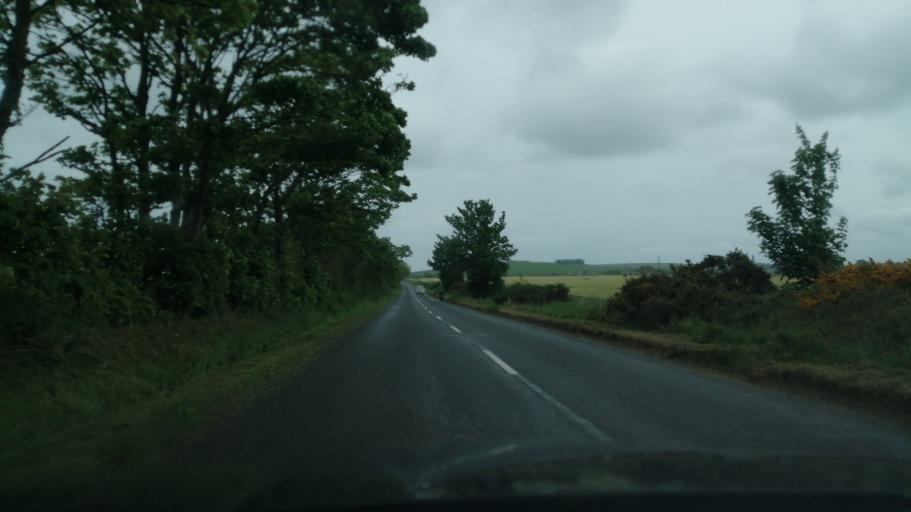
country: GB
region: Scotland
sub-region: Aberdeenshire
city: Portsoy
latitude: 57.6626
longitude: -2.6958
